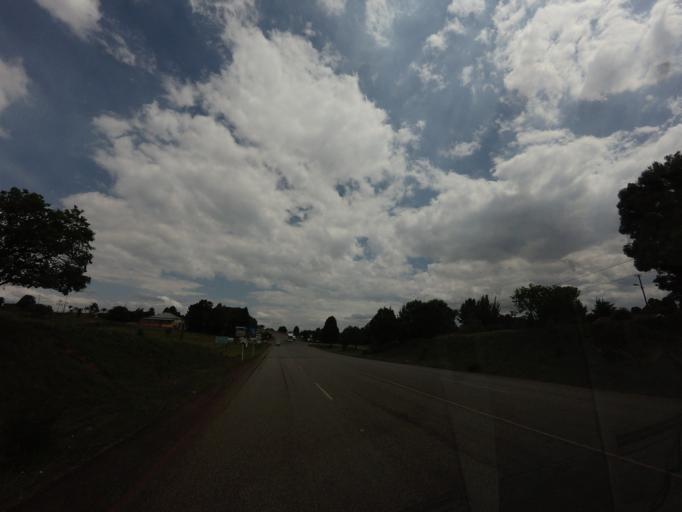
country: ZA
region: Mpumalanga
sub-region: Ehlanzeni District
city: Graksop
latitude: -24.9304
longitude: 30.8377
